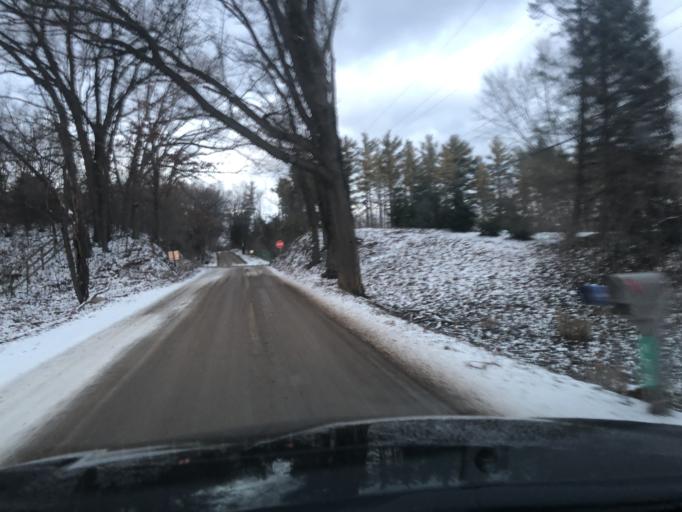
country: US
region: Michigan
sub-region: Oakland County
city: Milford
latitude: 42.5779
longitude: -83.6394
